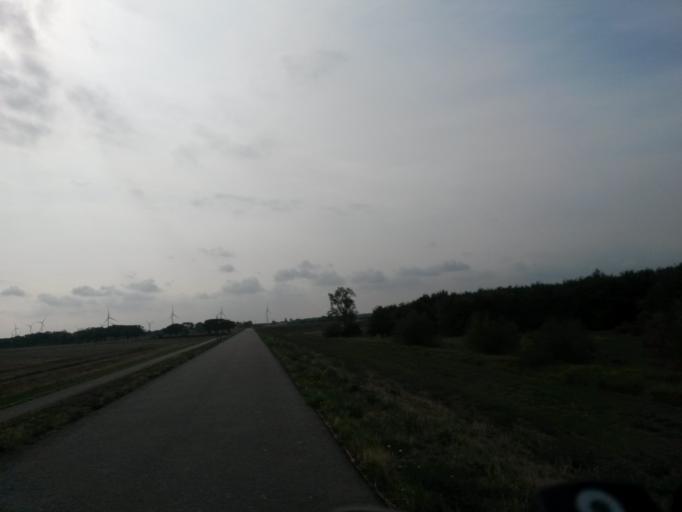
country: DE
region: Saxony-Anhalt
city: Tangermunde
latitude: 52.5496
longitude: 12.0005
